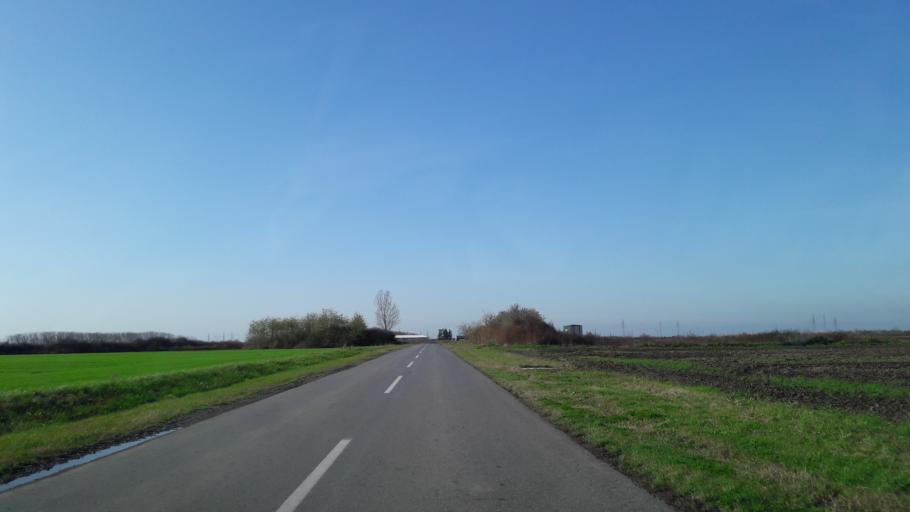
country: HR
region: Osjecko-Baranjska
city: Antunovac
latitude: 45.4757
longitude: 18.6900
